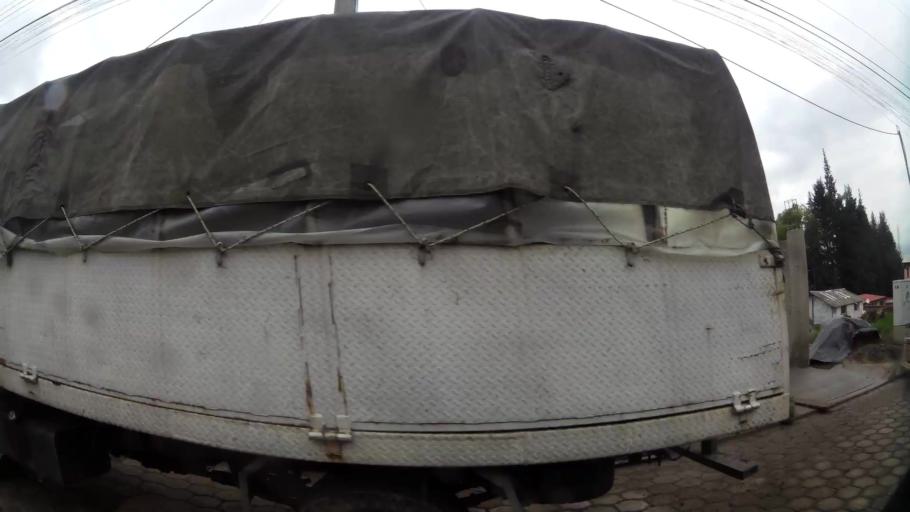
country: EC
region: Pichincha
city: Sangolqui
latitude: -0.3231
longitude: -78.4359
